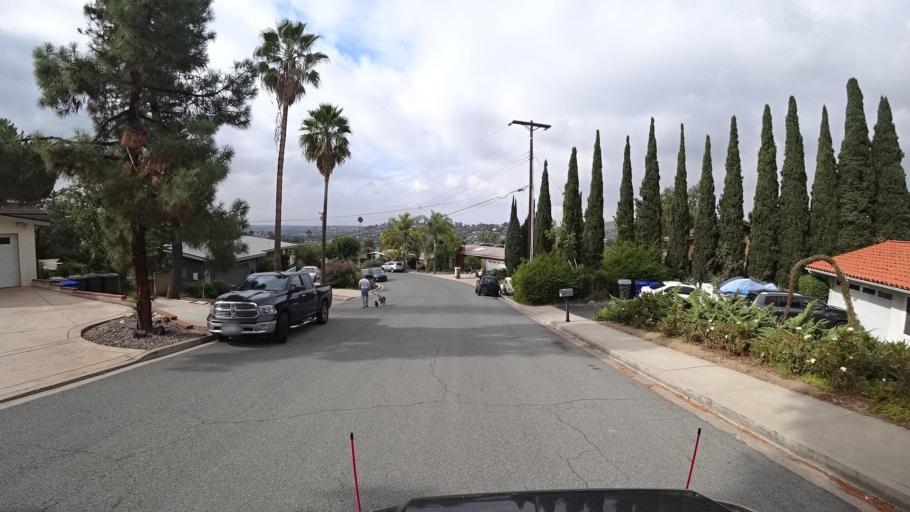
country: US
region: California
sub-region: San Diego County
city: Spring Valley
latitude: 32.7532
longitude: -116.9951
